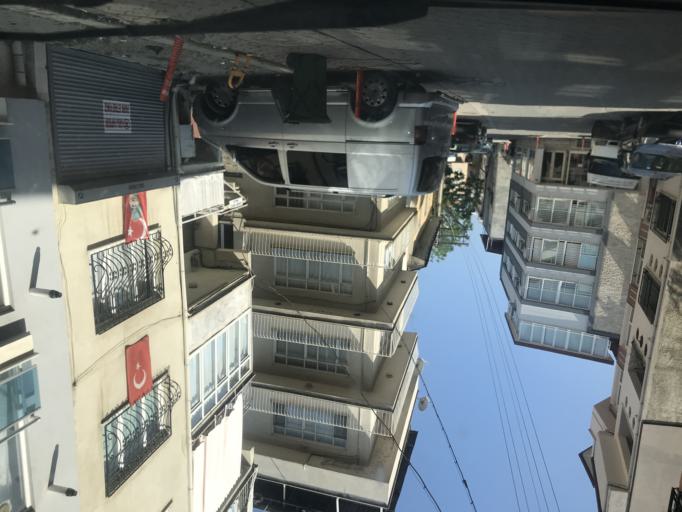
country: TR
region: Denizli
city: Denizli
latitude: 37.7730
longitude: 29.0837
